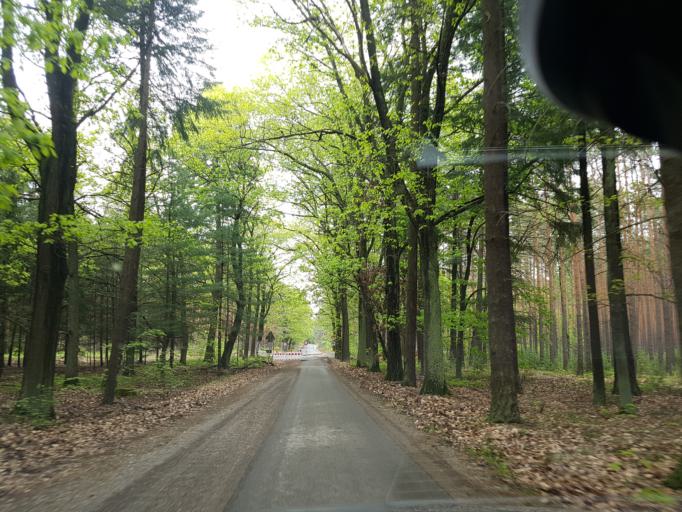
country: DE
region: Brandenburg
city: Crinitz
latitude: 51.7045
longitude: 13.7785
